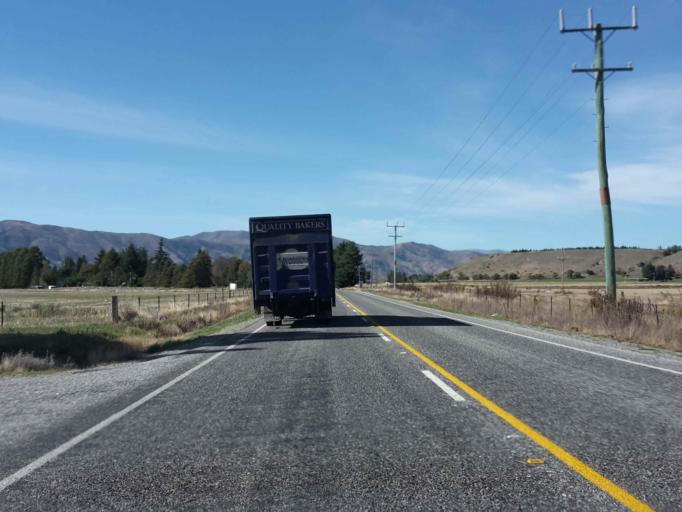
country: NZ
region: Otago
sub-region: Queenstown-Lakes District
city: Wanaka
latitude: -44.7198
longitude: 169.2251
